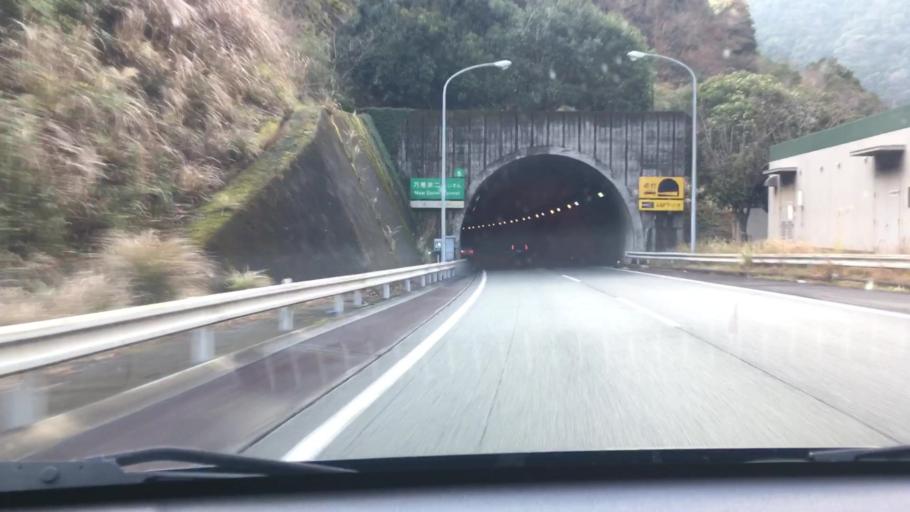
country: JP
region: Kumamoto
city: Hitoyoshi
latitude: 32.3162
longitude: 130.7517
